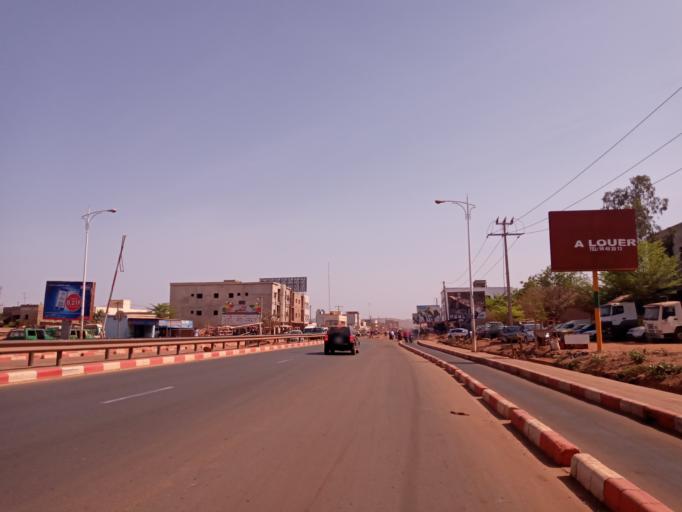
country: ML
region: Bamako
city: Bamako
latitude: 12.6340
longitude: -7.9226
